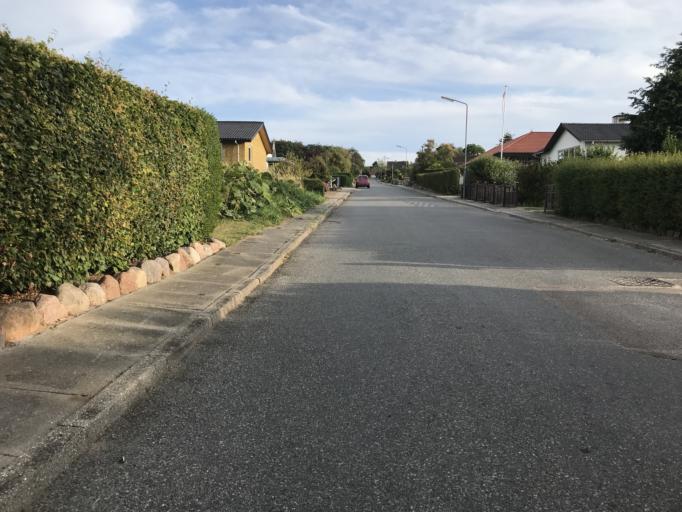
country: DK
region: South Denmark
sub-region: Faaborg-Midtfyn Kommune
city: Faaborg
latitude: 54.9406
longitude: 10.2613
